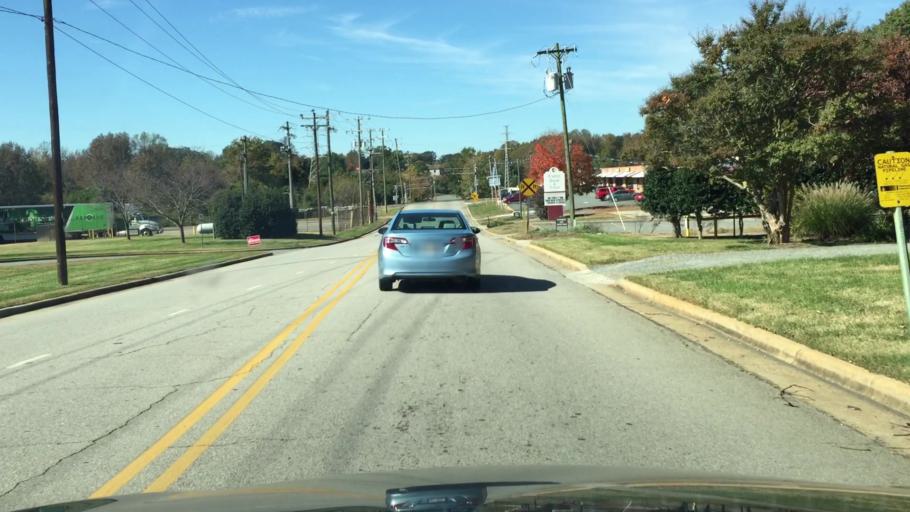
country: US
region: North Carolina
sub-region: Rockingham County
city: Reidsville
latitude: 36.3389
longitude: -79.6533
